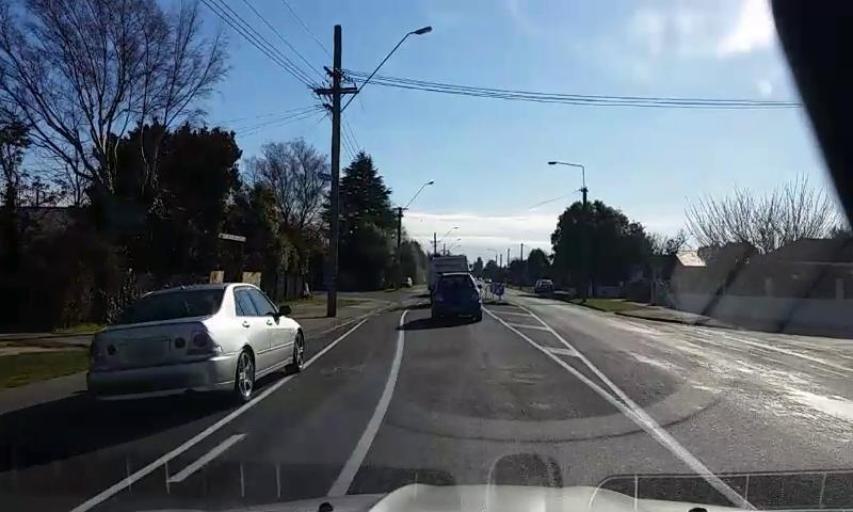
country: NZ
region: Canterbury
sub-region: Christchurch City
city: Christchurch
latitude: -43.4986
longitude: 172.6619
